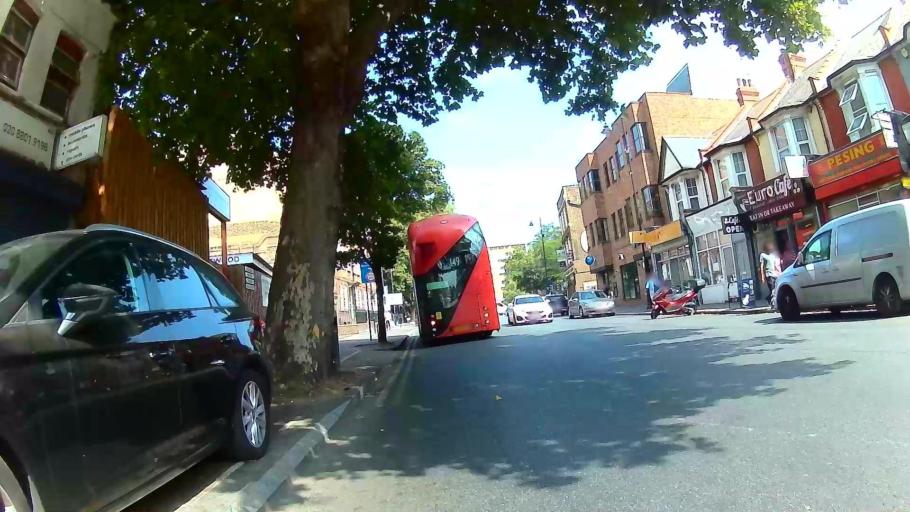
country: GB
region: England
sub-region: Greater London
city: Harringay
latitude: 51.6071
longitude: -0.0681
